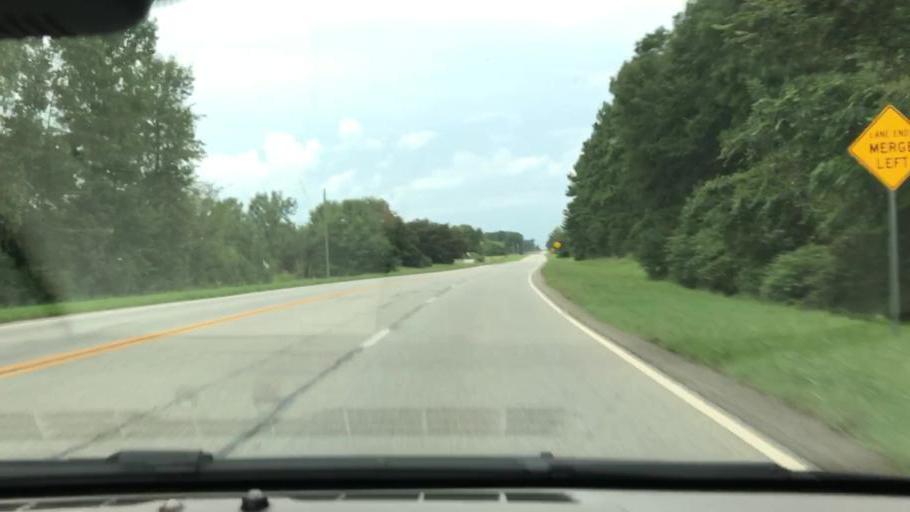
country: US
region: Georgia
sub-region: Early County
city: Blakely
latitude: 31.3319
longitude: -84.9945
